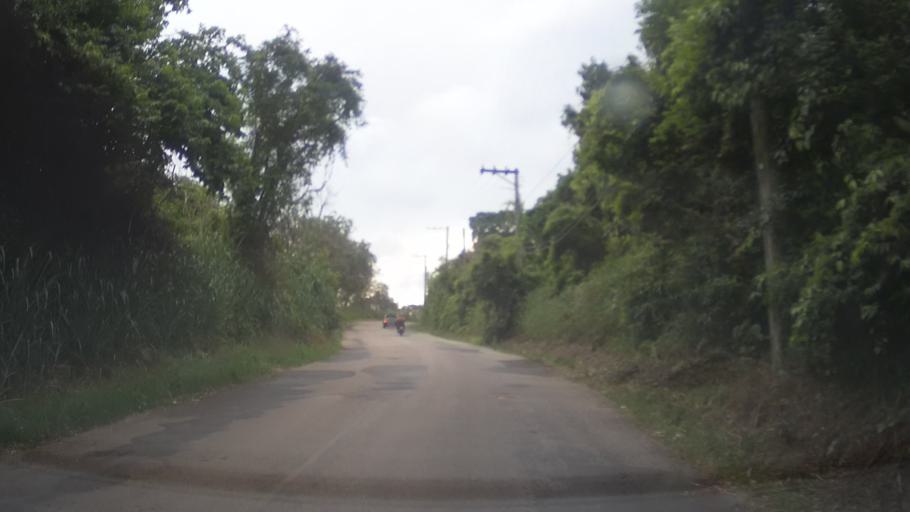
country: BR
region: Sao Paulo
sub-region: Itupeva
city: Itupeva
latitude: -23.1681
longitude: -47.0927
